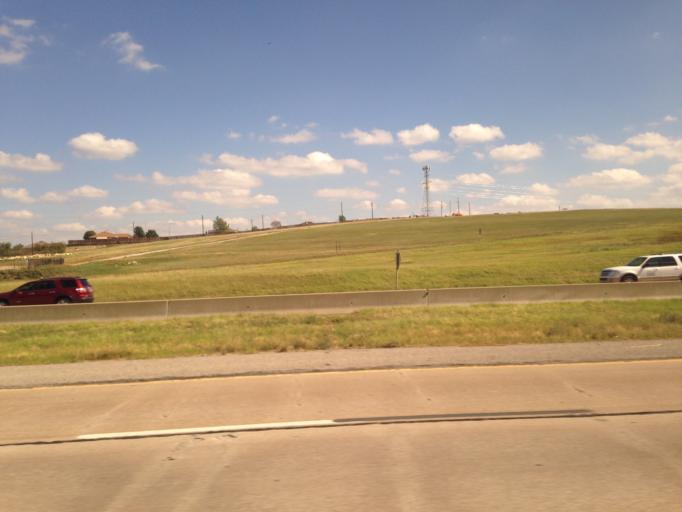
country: US
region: Texas
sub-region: Tarrant County
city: White Settlement
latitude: 32.7470
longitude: -97.4808
